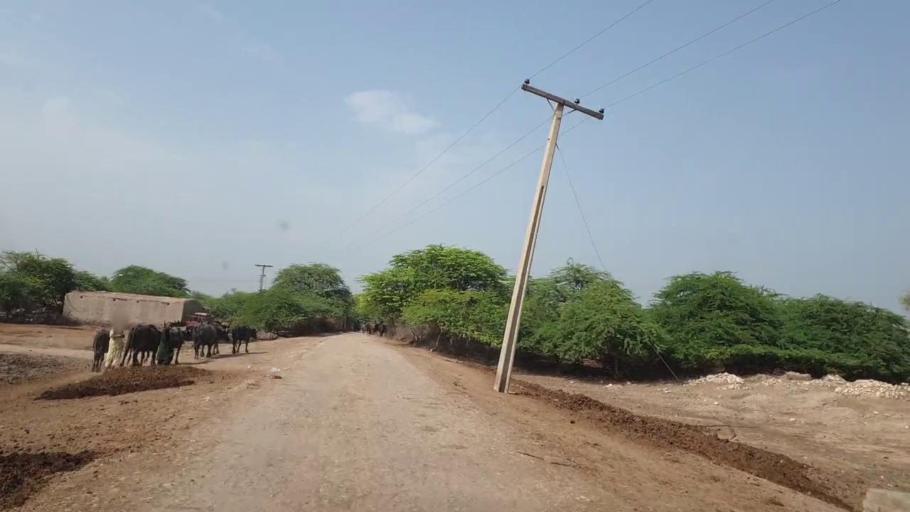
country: PK
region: Sindh
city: Lakhi
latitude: 27.8131
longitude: 68.7277
